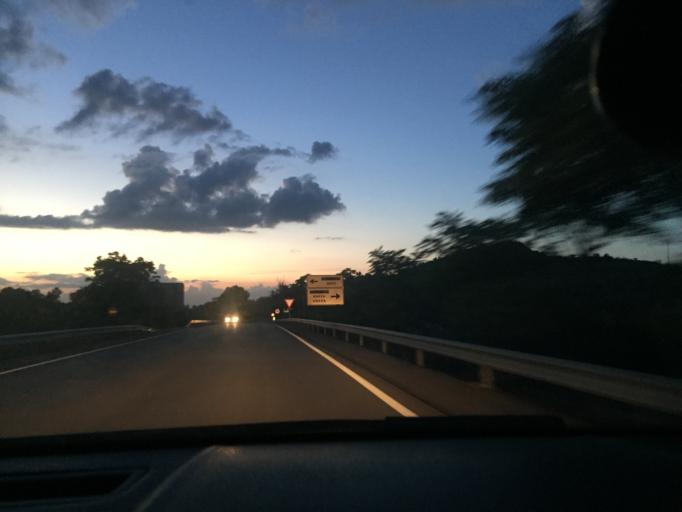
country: ES
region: Andalusia
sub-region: Provincia de Jaen
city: Mancha Real
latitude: 37.8000
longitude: -3.6578
